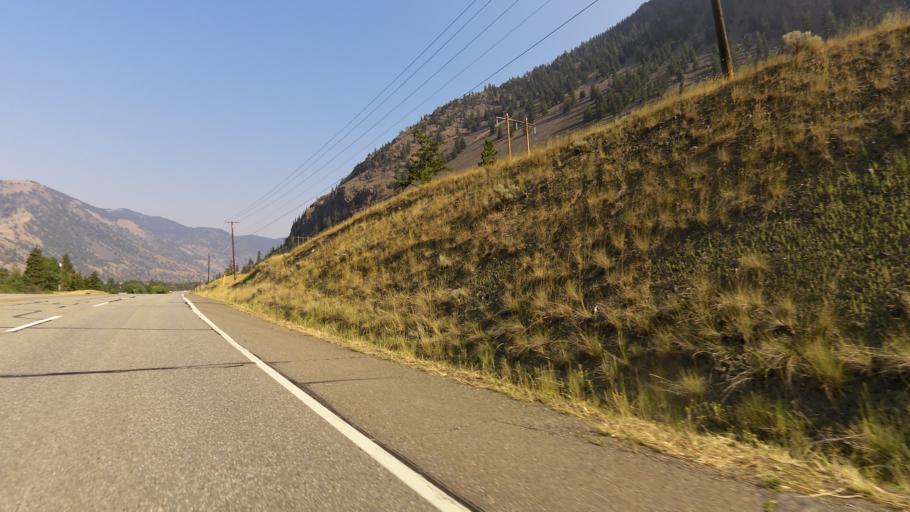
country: CA
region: British Columbia
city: Oliver
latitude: 49.2358
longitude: -119.9925
